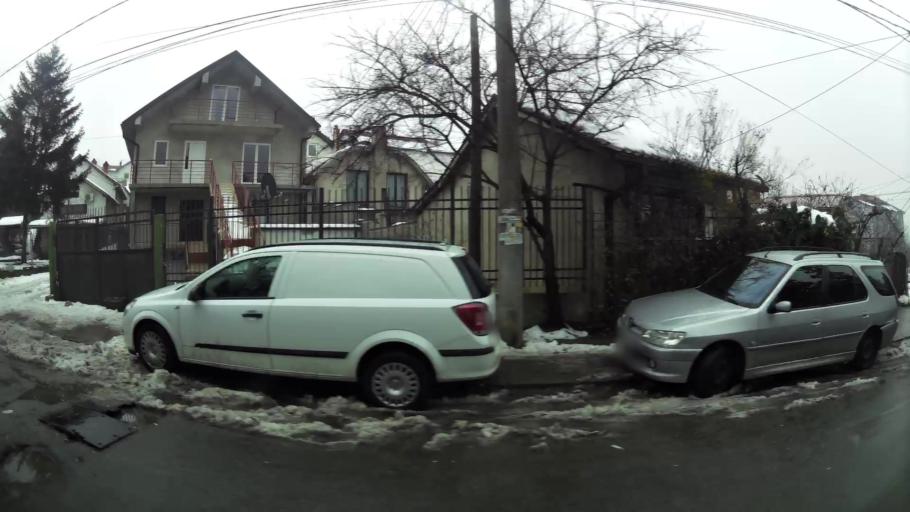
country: RS
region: Central Serbia
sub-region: Belgrade
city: Zvezdara
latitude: 44.7822
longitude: 20.5165
